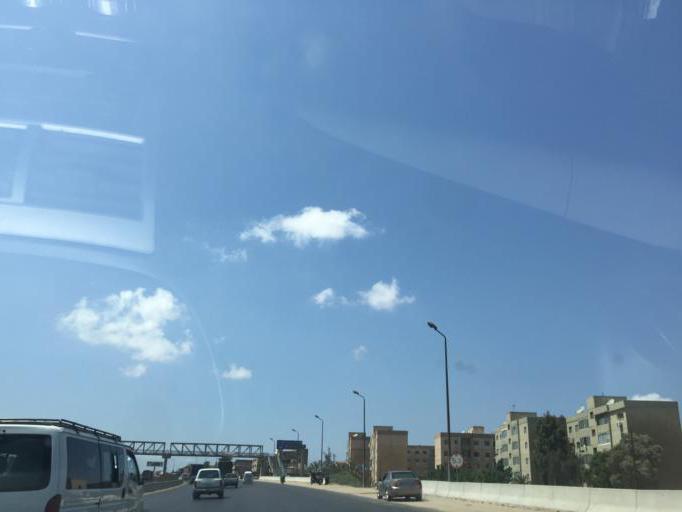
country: EG
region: Alexandria
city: Alexandria
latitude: 31.0245
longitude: 29.7927
